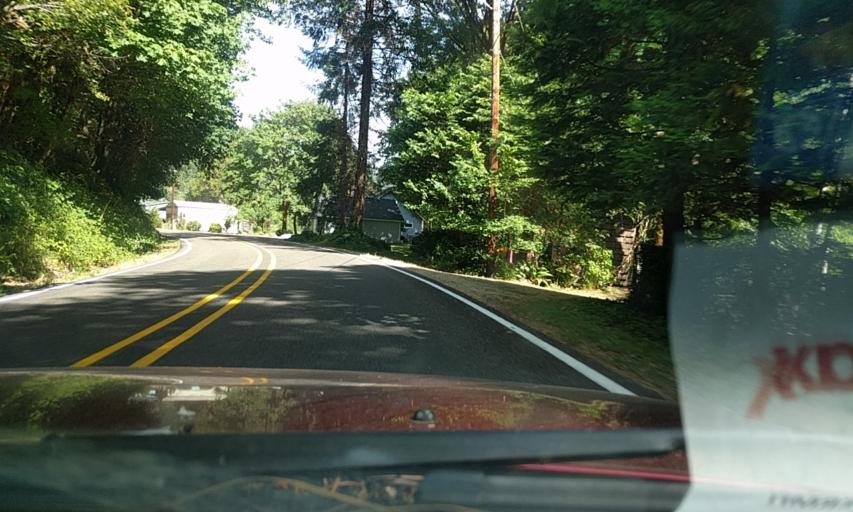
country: US
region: Oregon
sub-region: Lane County
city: Florence
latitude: 44.0420
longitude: -123.8731
